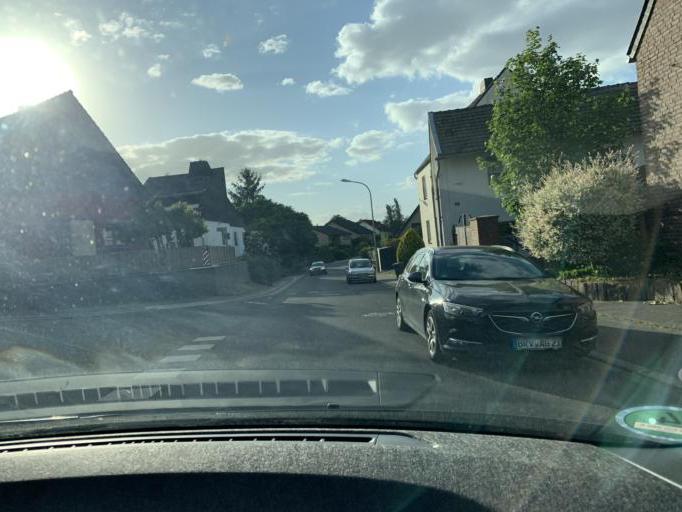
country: DE
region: North Rhine-Westphalia
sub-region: Regierungsbezirk Koln
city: Kreuzau
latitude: 50.7624
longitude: 6.4589
